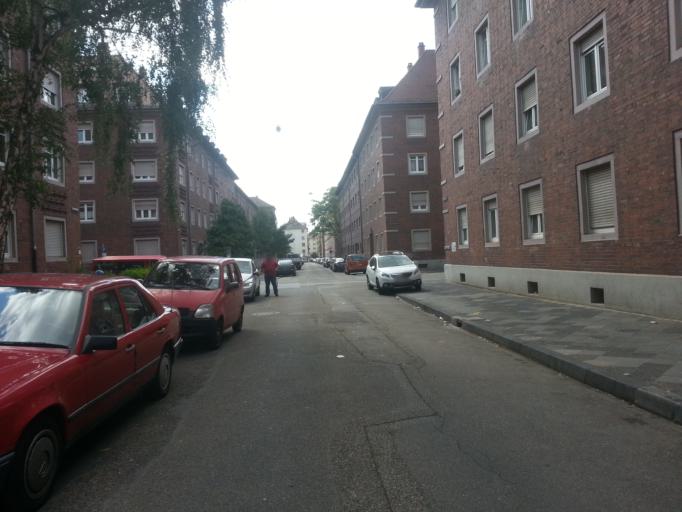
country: DE
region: Baden-Wuerttemberg
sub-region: Karlsruhe Region
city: Mannheim
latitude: 49.4997
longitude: 8.4934
